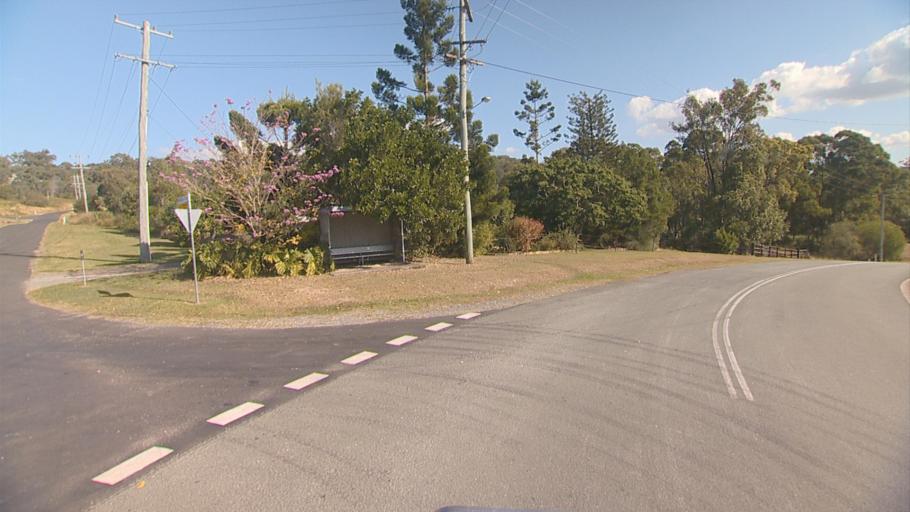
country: AU
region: Queensland
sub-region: Logan
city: Windaroo
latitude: -27.7398
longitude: 153.1731
